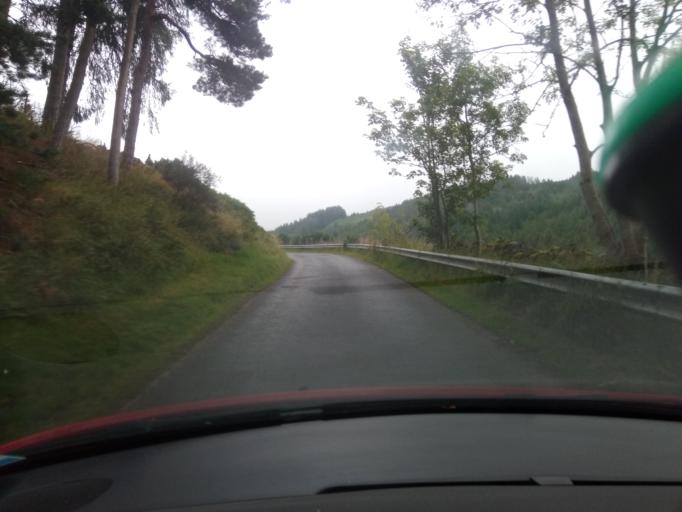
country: GB
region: Scotland
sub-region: The Scottish Borders
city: Galashiels
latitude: 55.7063
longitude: -2.8898
